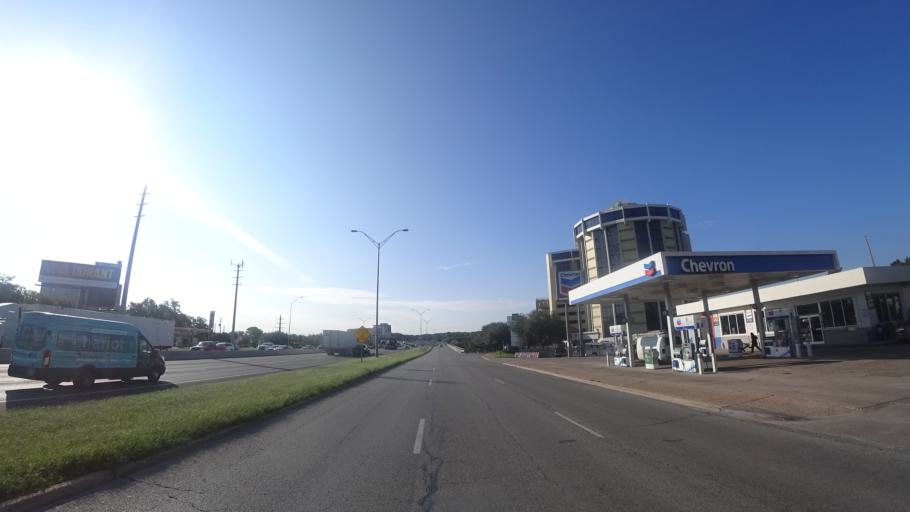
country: US
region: Texas
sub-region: Travis County
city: Austin
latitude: 30.2549
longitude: -97.7371
